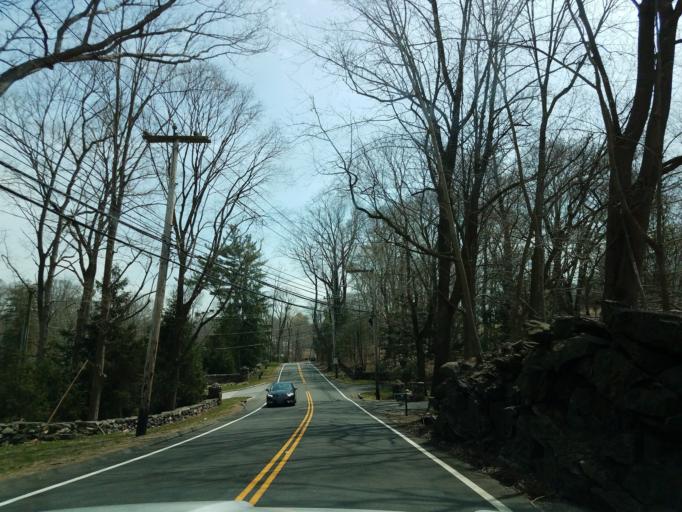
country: US
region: Connecticut
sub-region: Fairfield County
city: Glenville
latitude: 41.0361
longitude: -73.6488
